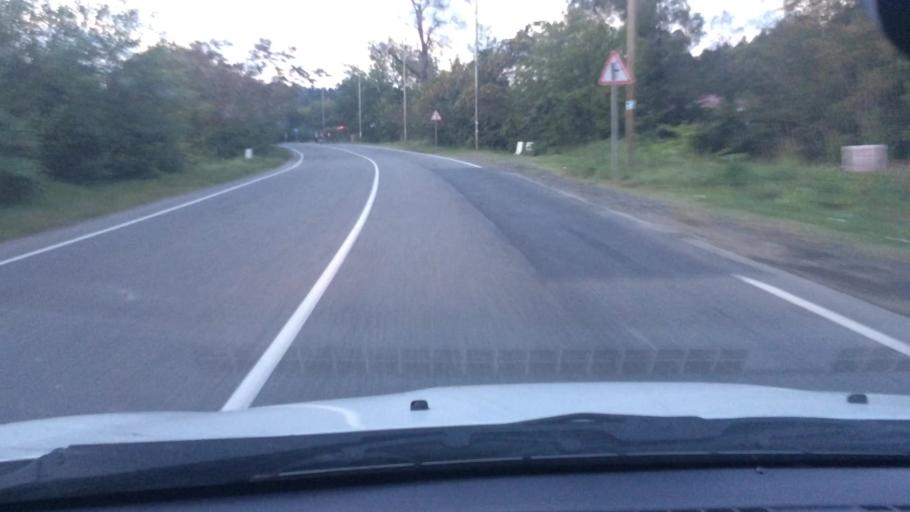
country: GE
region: Guria
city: Urek'i
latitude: 41.9844
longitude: 41.7841
